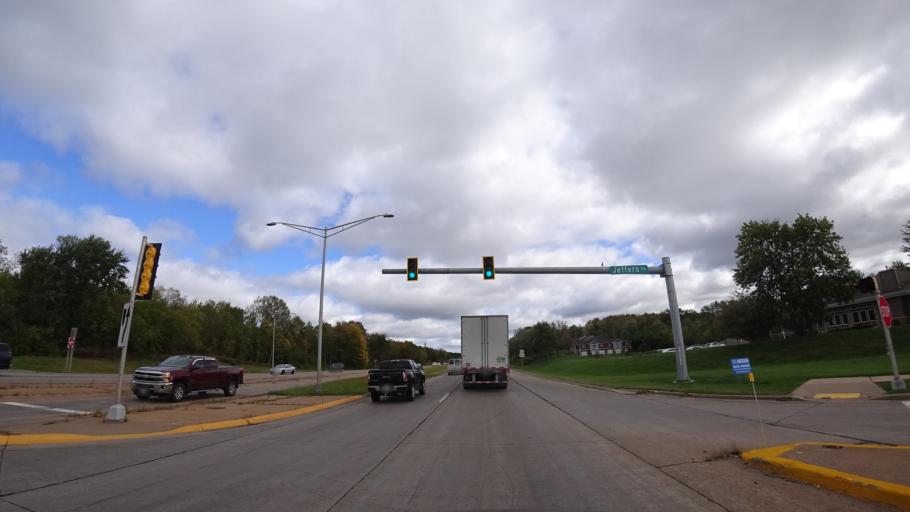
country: US
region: Wisconsin
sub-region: Eau Claire County
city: Eau Claire
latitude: 44.8423
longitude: -91.5244
